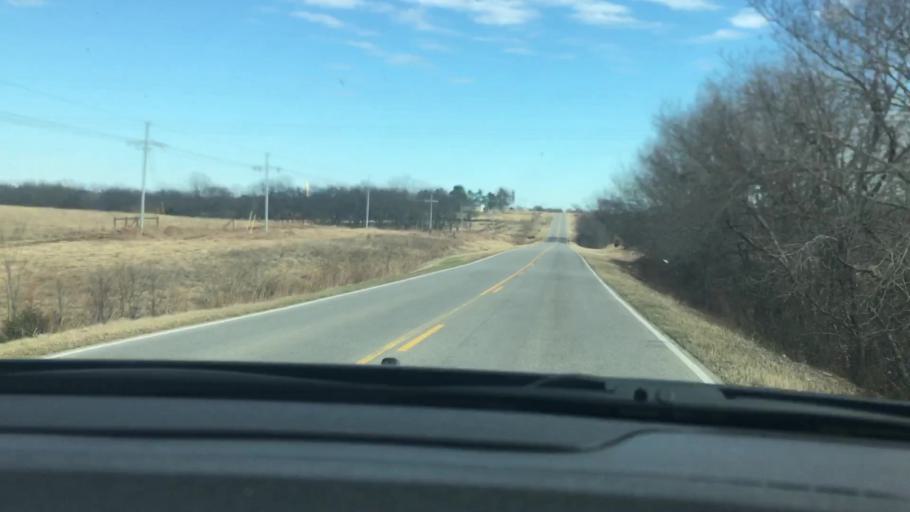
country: US
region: Oklahoma
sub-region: Garvin County
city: Stratford
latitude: 34.7968
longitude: -96.8280
